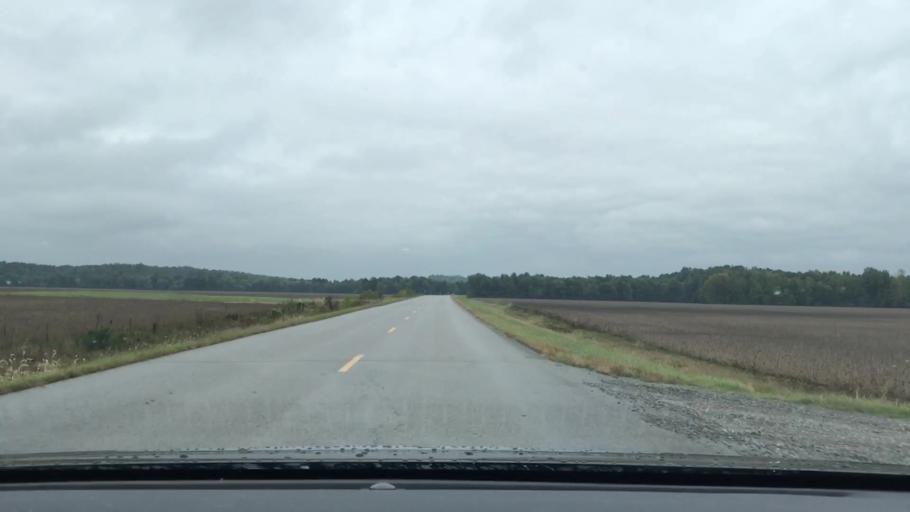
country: US
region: Kentucky
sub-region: McLean County
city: Calhoun
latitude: 37.4998
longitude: -87.2481
